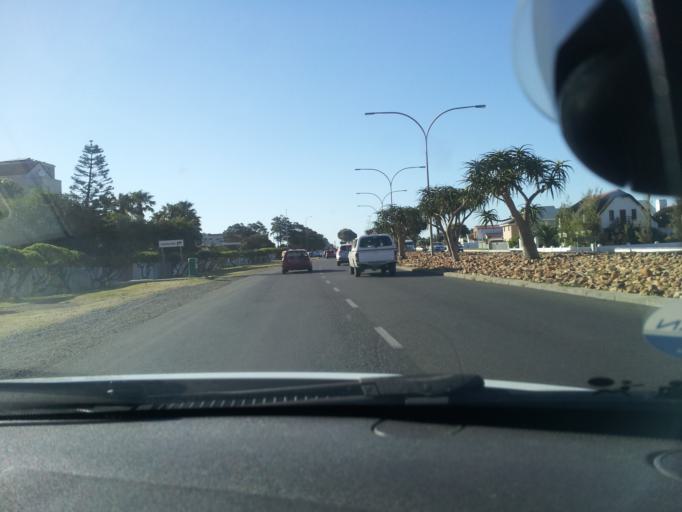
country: ZA
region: Western Cape
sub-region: Overberg District Municipality
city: Grabouw
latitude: -34.1496
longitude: 18.8594
